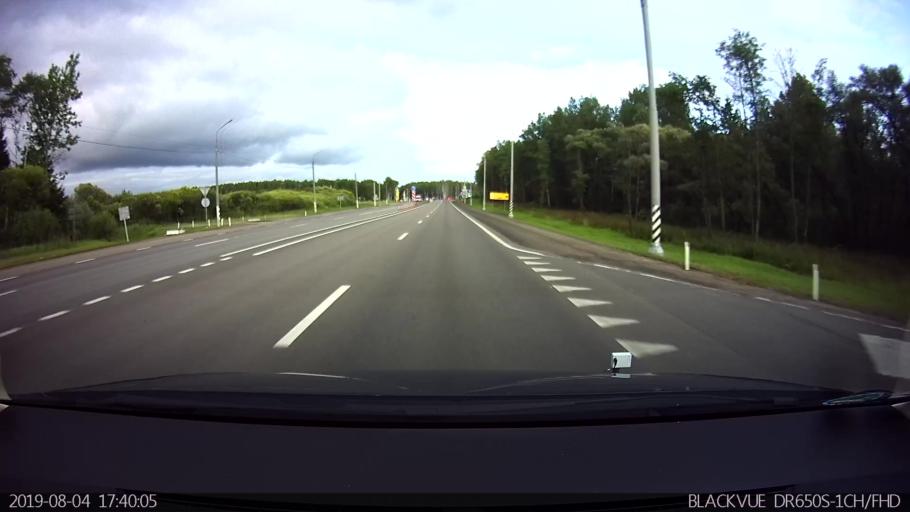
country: RU
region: Moskovskaya
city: Uvarovka
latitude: 55.4921
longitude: 35.3075
